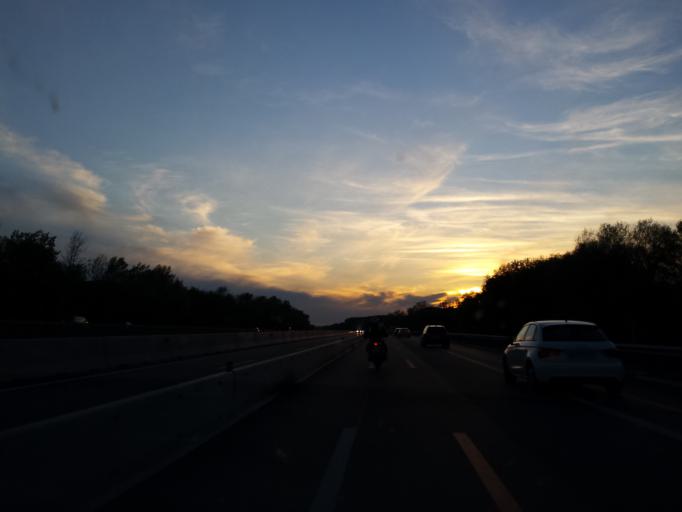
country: AT
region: Lower Austria
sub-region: Politischer Bezirk Wien-Umgebung
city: Fischamend Dorf
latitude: 48.1272
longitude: 16.5875
